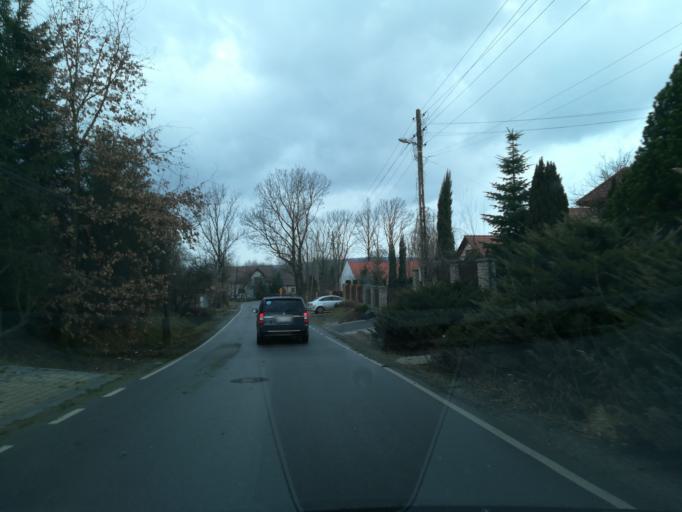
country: PL
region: Lesser Poland Voivodeship
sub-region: Krakow
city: Sidzina
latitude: 49.9834
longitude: 19.8733
